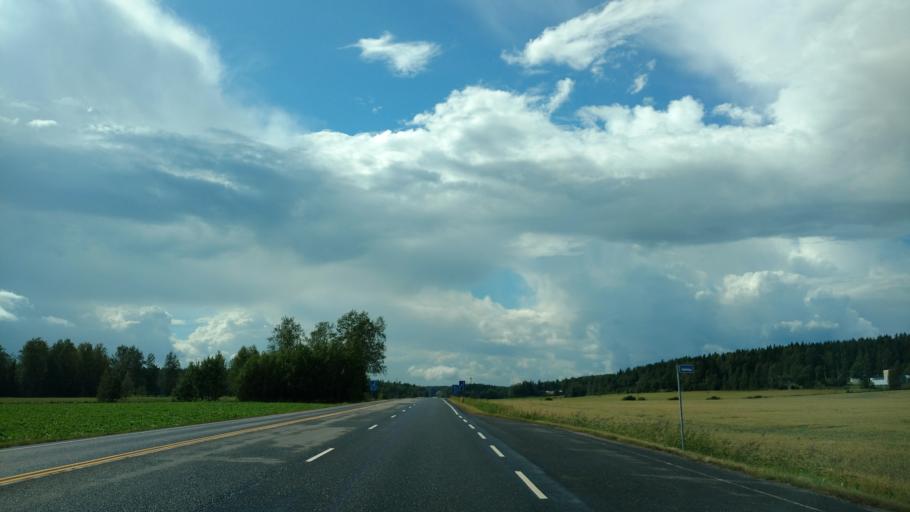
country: FI
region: Varsinais-Suomi
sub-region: Salo
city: Halikko
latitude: 60.3761
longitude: 22.9682
